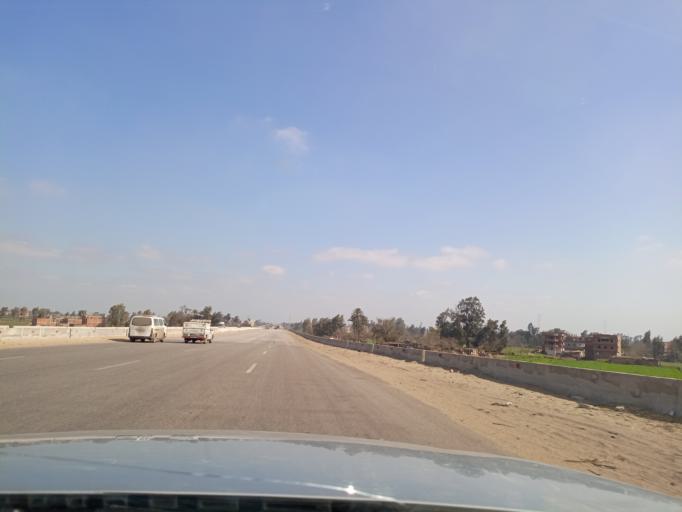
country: EG
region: Muhafazat al Minufiyah
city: Al Bajur
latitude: 30.4249
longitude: 31.0908
